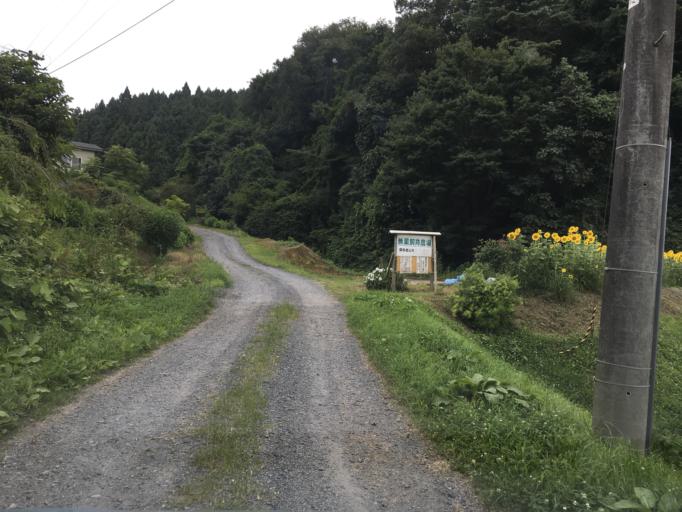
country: JP
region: Iwate
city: Ichinoseki
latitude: 38.8612
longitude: 141.3675
